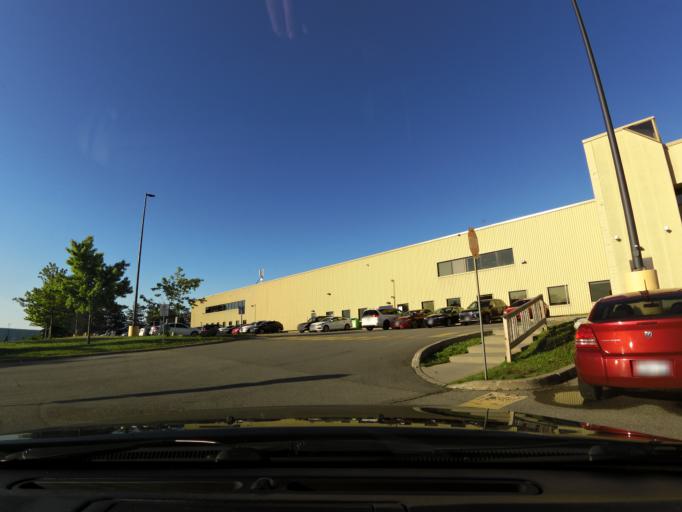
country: CA
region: Ontario
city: Mississauga
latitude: 43.6015
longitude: -79.7374
